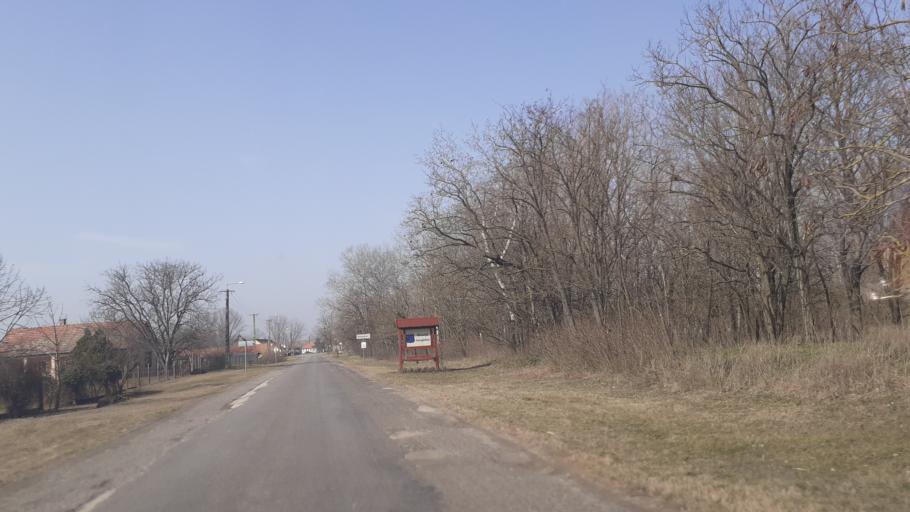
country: HU
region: Pest
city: Dabas
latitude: 47.0632
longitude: 19.2840
